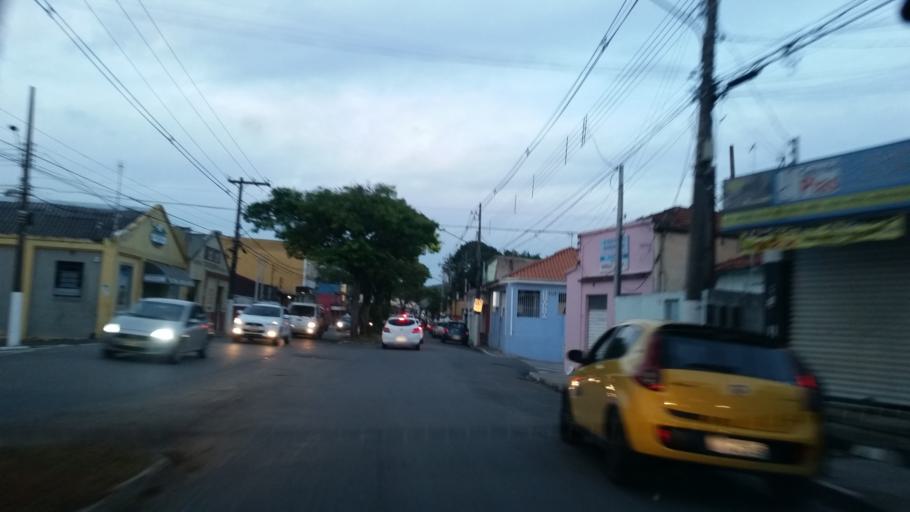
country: BR
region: Sao Paulo
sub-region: Atibaia
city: Atibaia
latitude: -23.1092
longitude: -46.5577
